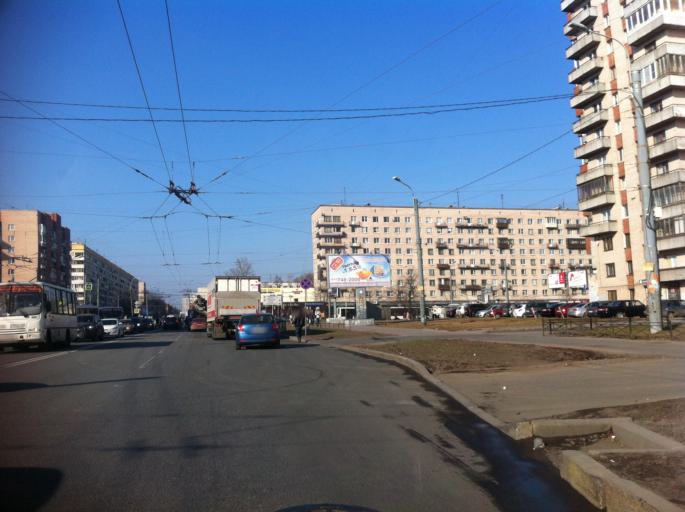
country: RU
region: St.-Petersburg
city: Dachnoye
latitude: 59.8508
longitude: 30.2564
